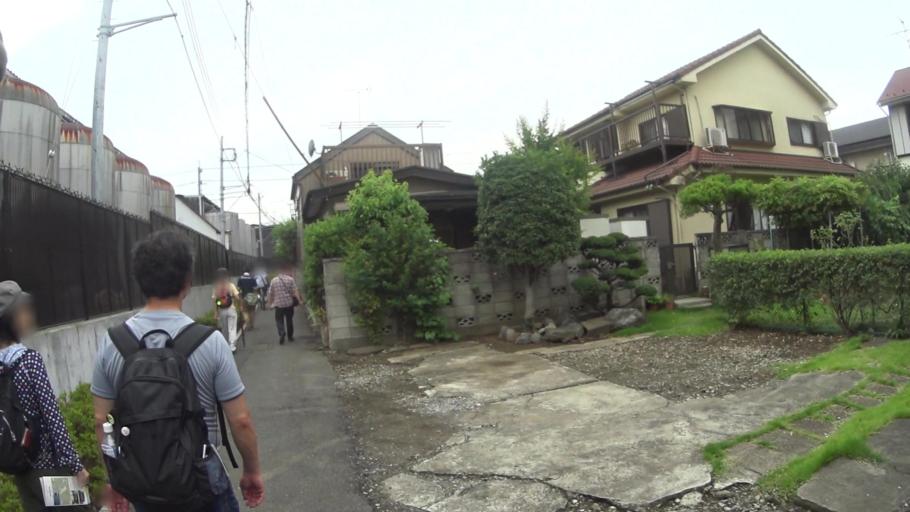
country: JP
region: Chiba
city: Nagareyama
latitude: 35.8549
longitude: 139.8988
